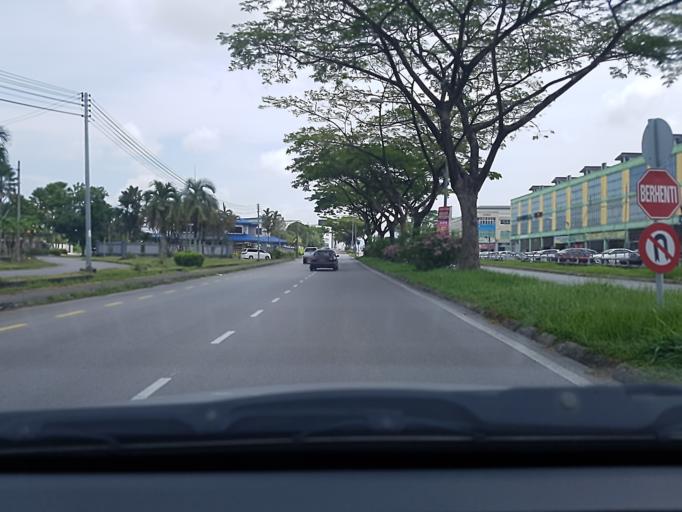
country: MY
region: Sarawak
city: Kuching
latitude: 1.5186
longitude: 110.3608
